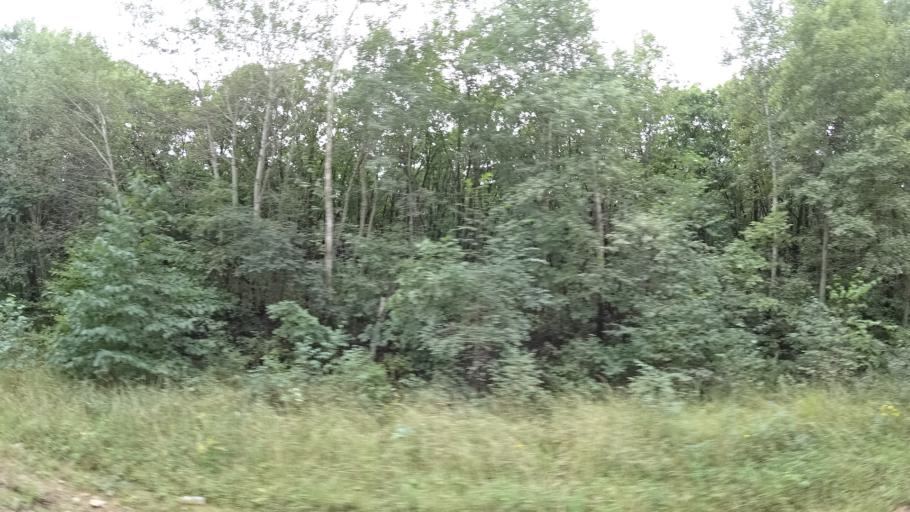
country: RU
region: Primorskiy
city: Lyalichi
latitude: 44.0842
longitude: 132.4438
